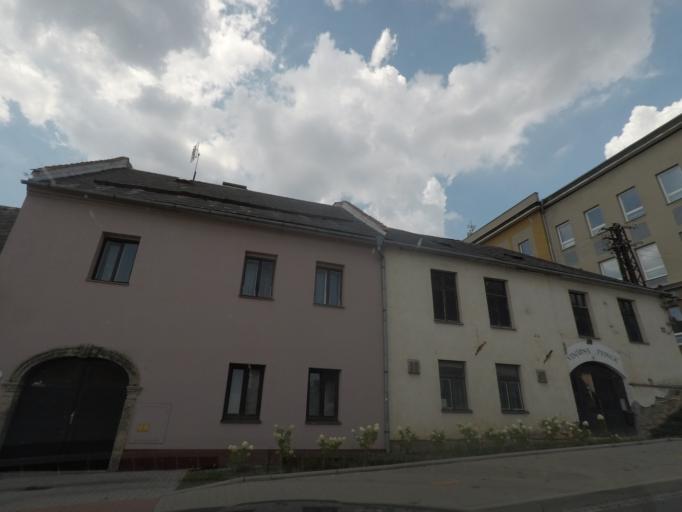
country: CZ
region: Olomoucky
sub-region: Okres Sumperk
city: Mohelnice
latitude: 49.7739
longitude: 16.9181
